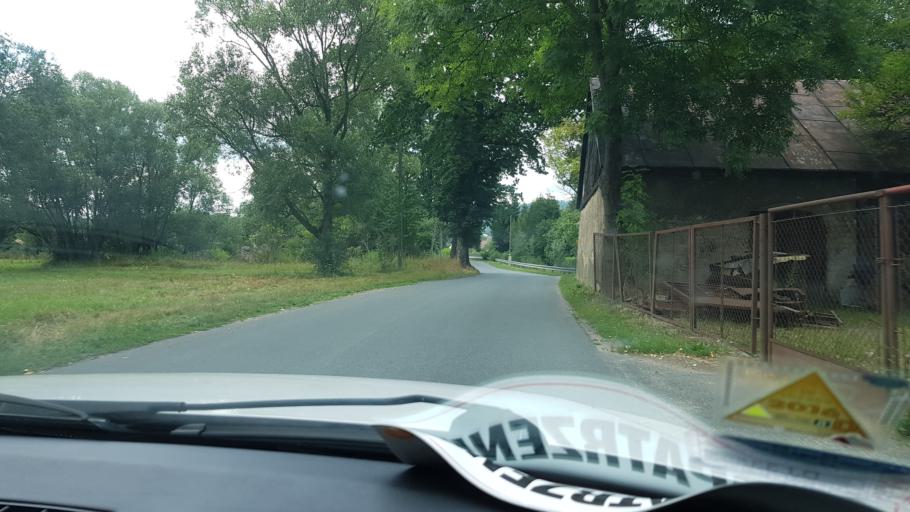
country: PL
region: Lower Silesian Voivodeship
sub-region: Powiat jeleniogorski
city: Jezow Sudecki
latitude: 50.9303
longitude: 15.7981
